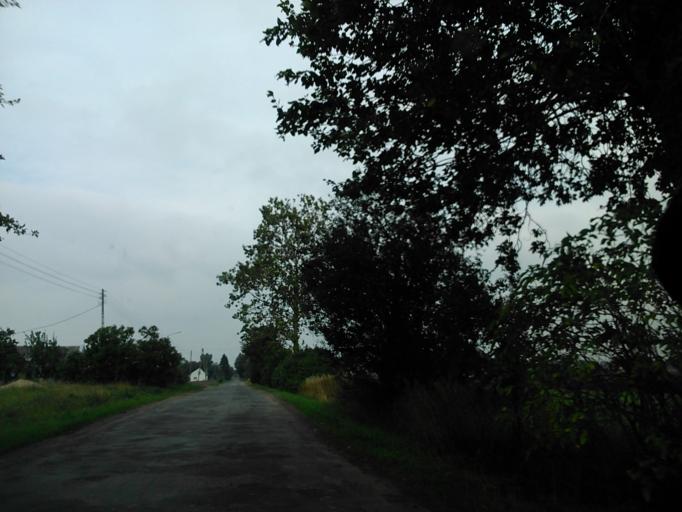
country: PL
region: Kujawsko-Pomorskie
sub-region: Powiat wabrzeski
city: Pluznica
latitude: 53.2505
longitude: 18.8251
